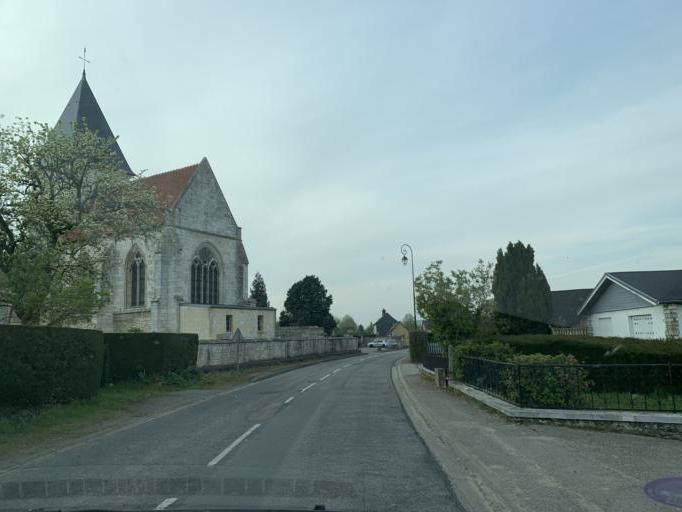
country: FR
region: Haute-Normandie
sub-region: Departement de la Seine-Maritime
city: La Mailleraye-sur-Seine
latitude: 49.4926
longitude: 0.7649
